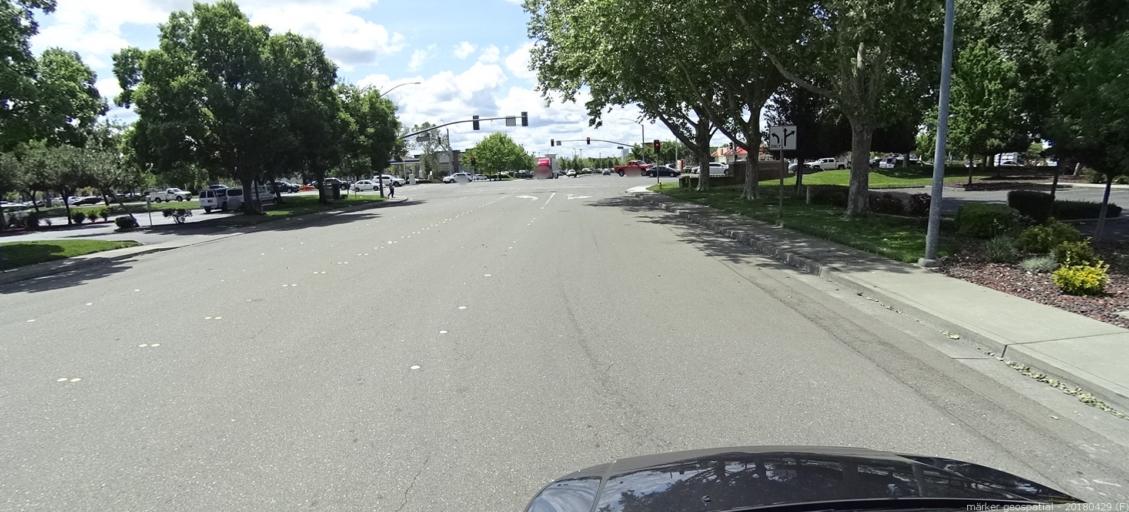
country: US
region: California
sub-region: Yolo County
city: West Sacramento
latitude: 38.5924
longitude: -121.5487
